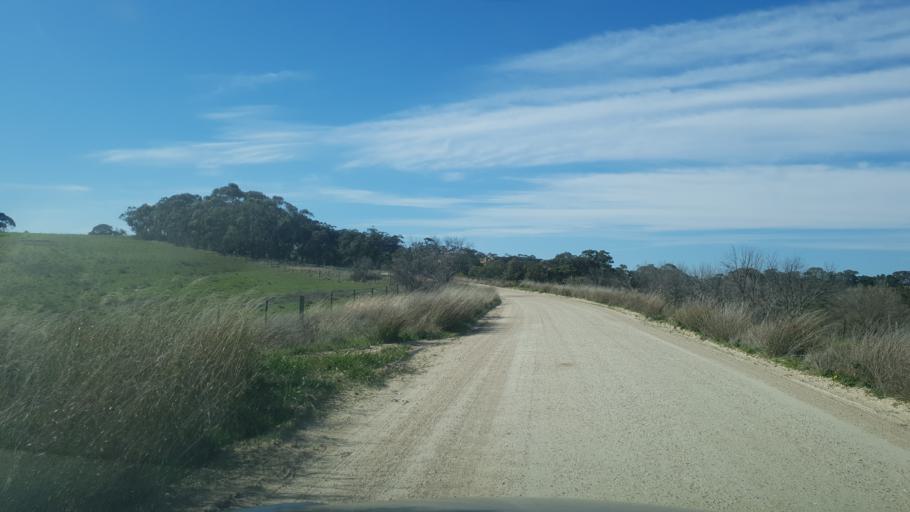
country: AU
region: South Australia
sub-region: Gawler
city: Gawler
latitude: -34.6400
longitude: 138.8072
